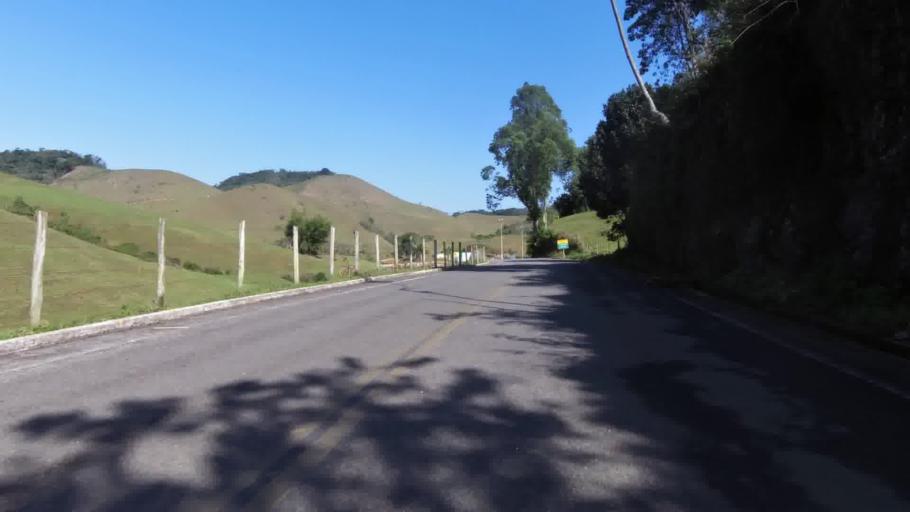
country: BR
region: Espirito Santo
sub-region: Alfredo Chaves
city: Alfredo Chaves
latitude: -20.5697
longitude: -40.8082
